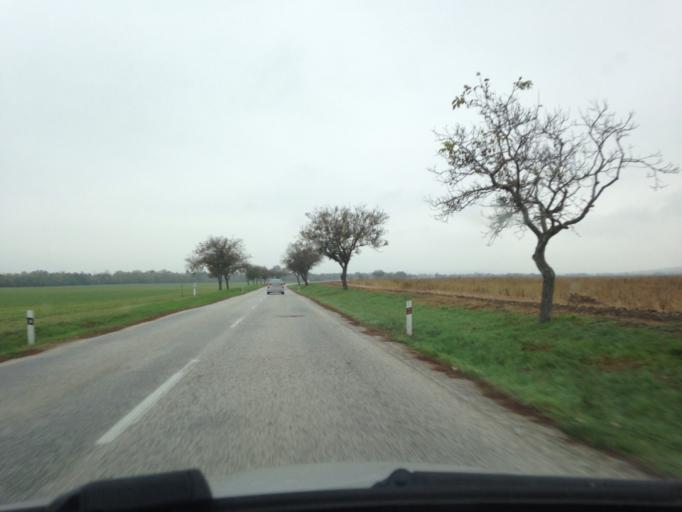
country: HU
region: Komarom-Esztergom
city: Nyergesujfalu
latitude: 47.8194
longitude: 18.5802
